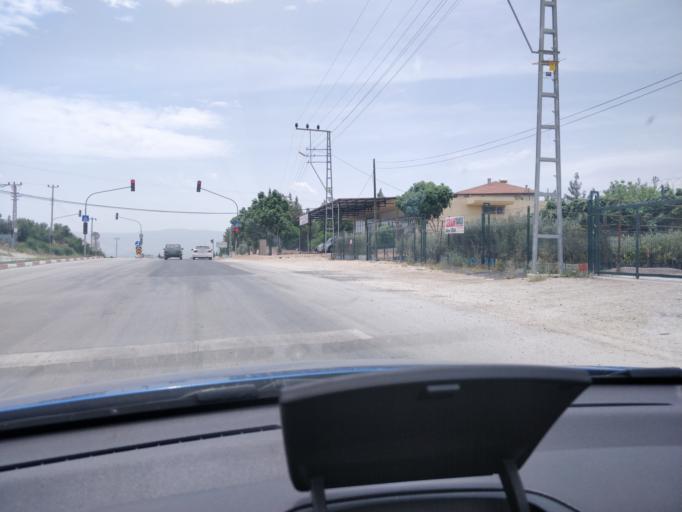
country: TR
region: Mersin
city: Mut
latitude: 36.6172
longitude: 33.4413
